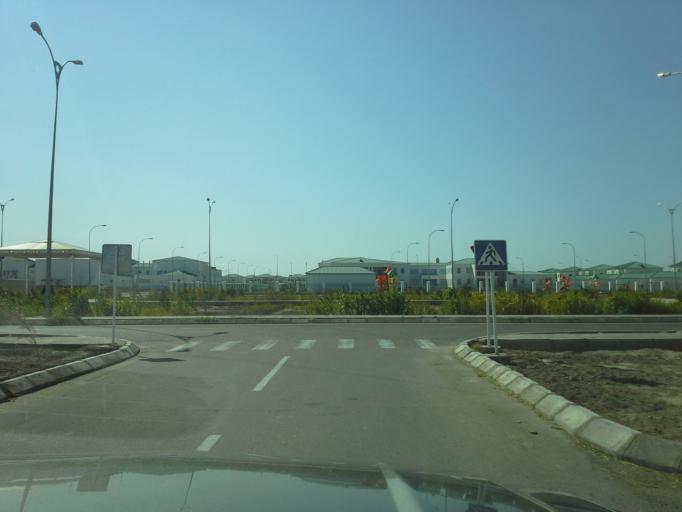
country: TM
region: Dasoguz
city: Dasoguz
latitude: 41.8145
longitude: 59.9572
